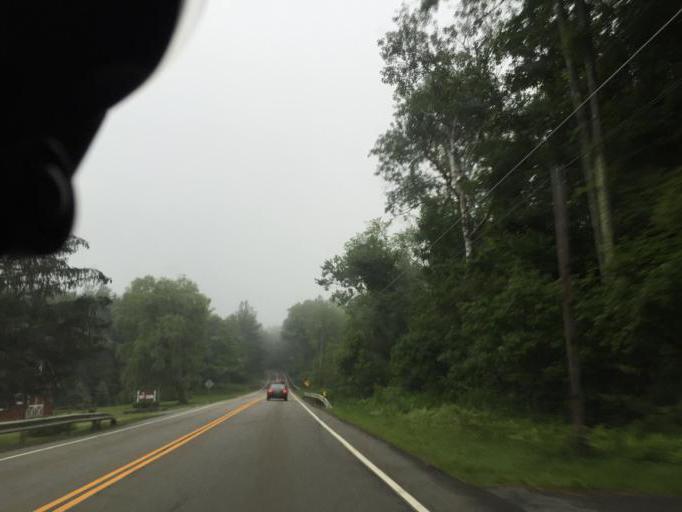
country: US
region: Connecticut
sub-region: Litchfield County
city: Winchester Center
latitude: 41.8892
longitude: -73.2554
